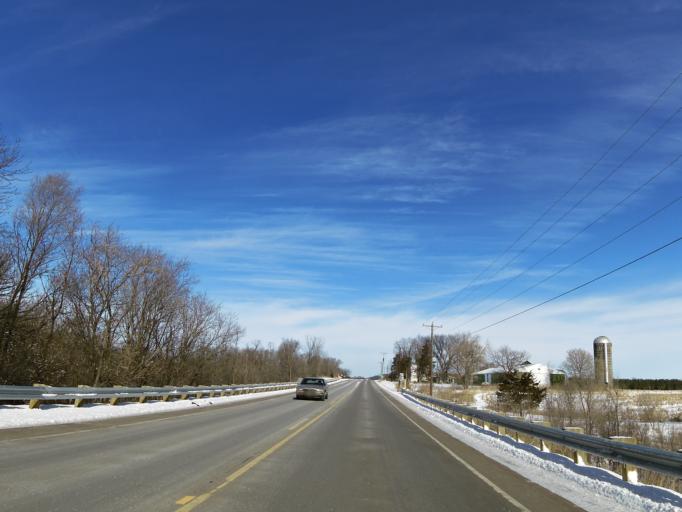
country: US
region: Minnesota
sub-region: Washington County
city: Afton
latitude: 44.8595
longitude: -92.7312
